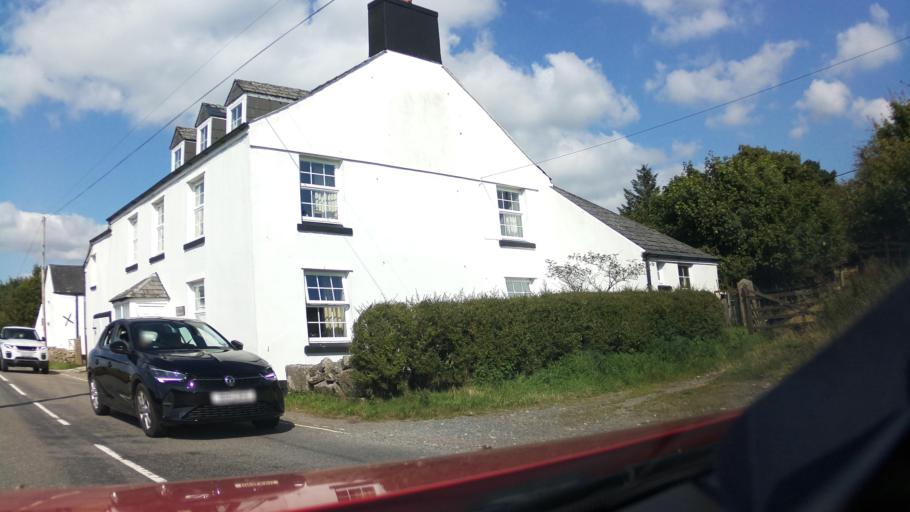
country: GB
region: England
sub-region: Devon
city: Yelverton
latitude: 50.5458
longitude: -3.9884
